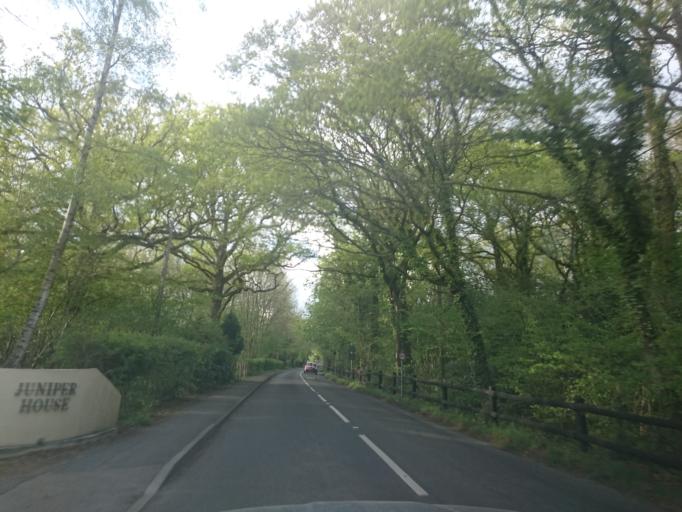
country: GB
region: England
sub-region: Surrey
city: Seale
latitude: 51.2403
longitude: -0.7094
